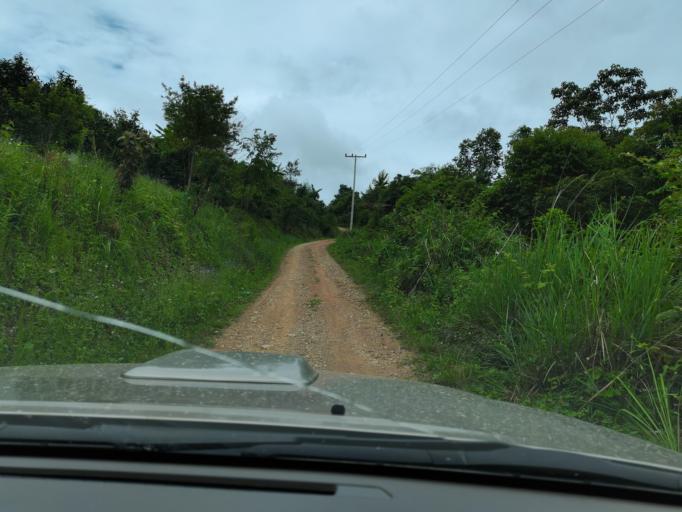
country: LA
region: Phongsali
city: Phongsali
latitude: 21.6622
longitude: 102.1757
